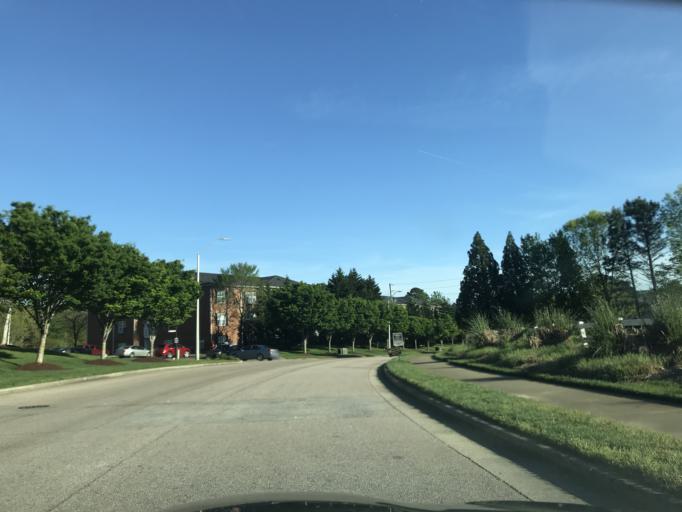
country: US
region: North Carolina
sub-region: Wake County
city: Knightdale
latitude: 35.8480
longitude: -78.5626
